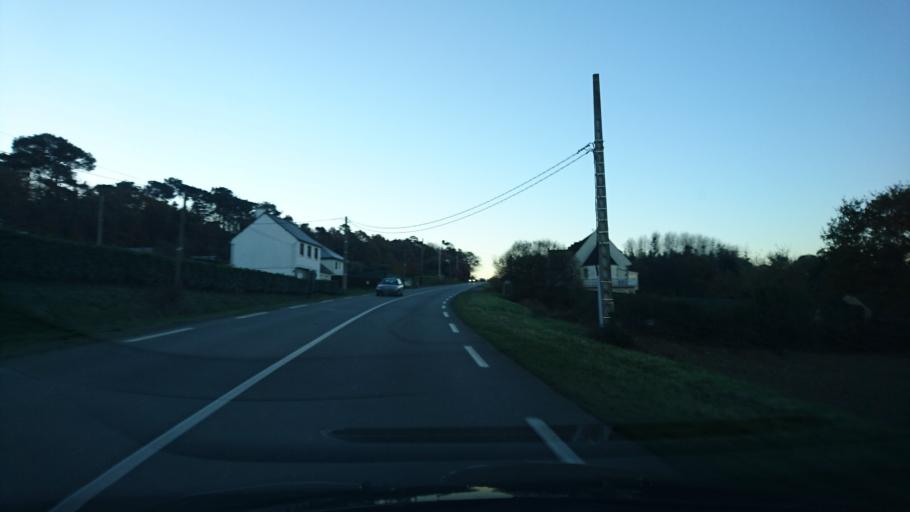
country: FR
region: Brittany
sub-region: Departement des Cotes-d'Armor
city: Pledran
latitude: 48.4561
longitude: -2.7536
